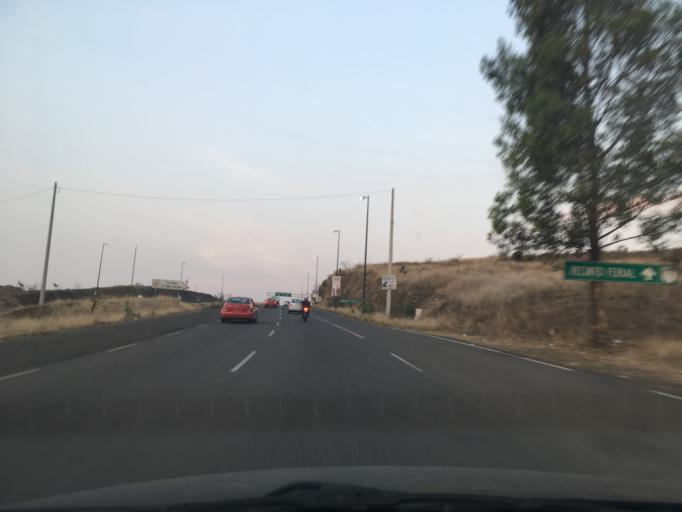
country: MX
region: Michoacan
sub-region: Morelia
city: La Aldea
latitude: 19.7295
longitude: -101.1045
